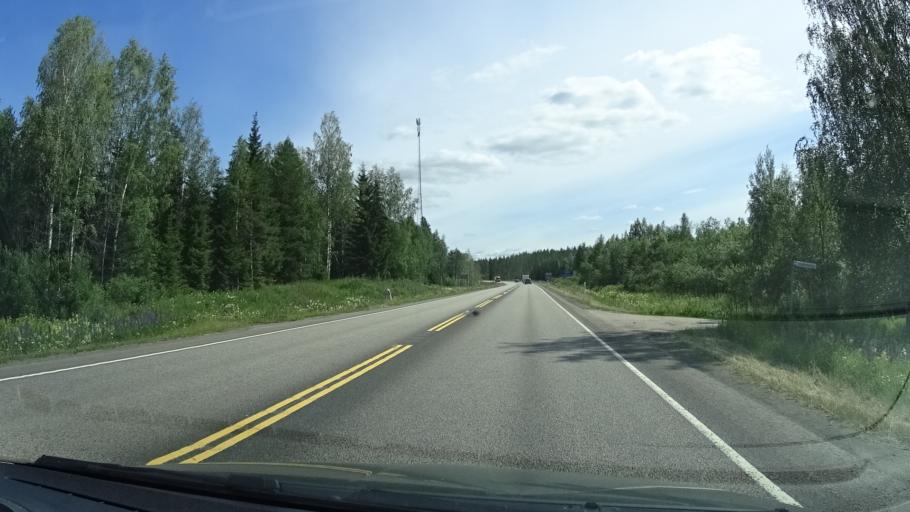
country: FI
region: Central Finland
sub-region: Jyvaeskylae
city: Uurainen
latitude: 62.2649
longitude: 25.4655
